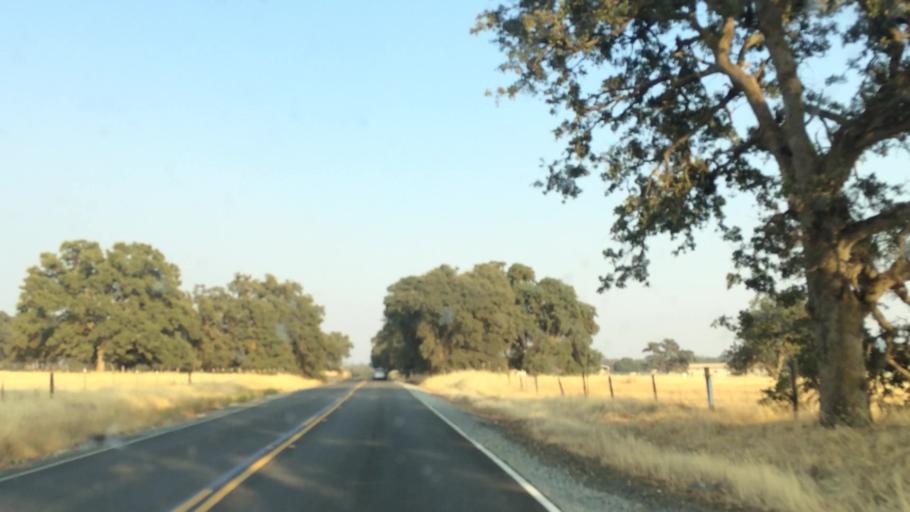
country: US
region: California
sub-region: Amador County
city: Ione
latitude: 38.3993
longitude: -121.0115
